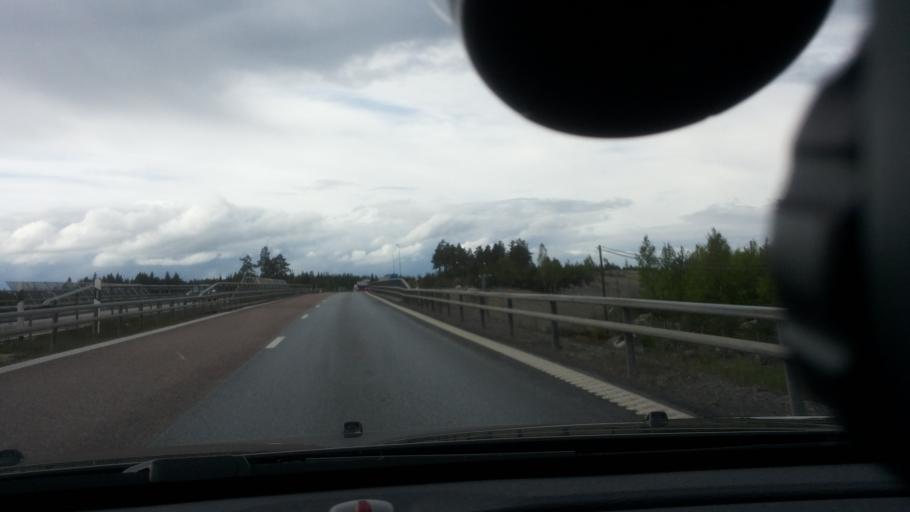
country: SE
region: Gaevleborg
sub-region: Soderhamns Kommun
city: Soderhamn
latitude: 61.3338
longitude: 17.0186
